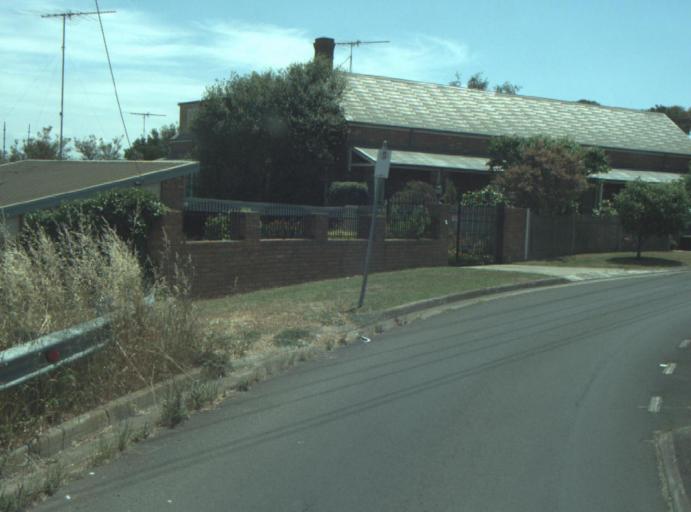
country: AU
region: Victoria
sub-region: Greater Geelong
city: Geelong West
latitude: -38.1483
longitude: 144.3272
